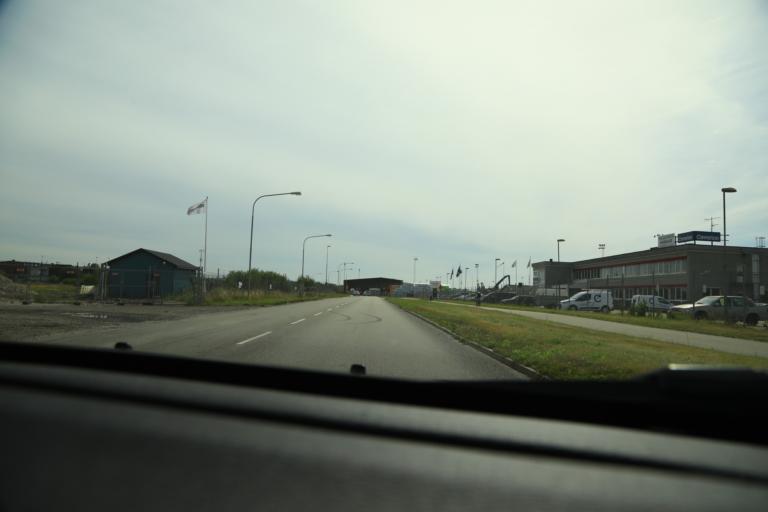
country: SE
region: Halland
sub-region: Varbergs Kommun
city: Varberg
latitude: 57.1172
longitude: 12.2486
